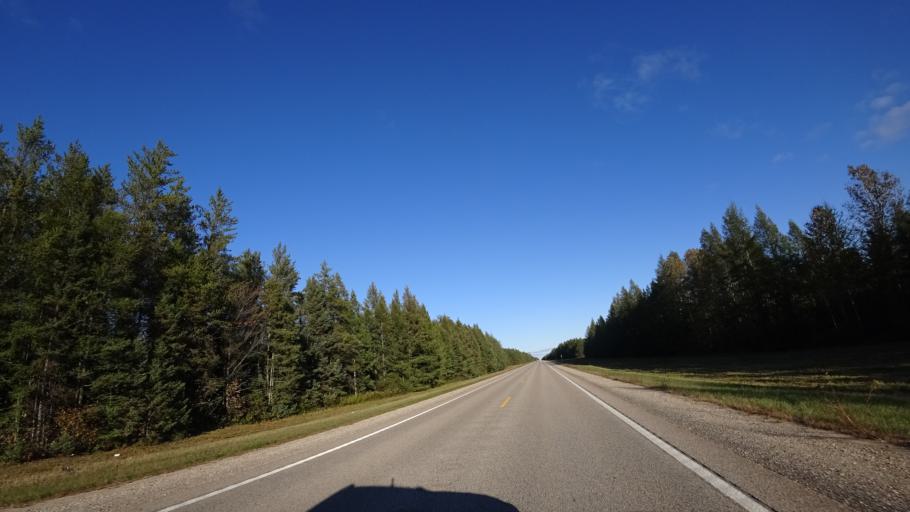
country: US
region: Michigan
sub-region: Alger County
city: Munising
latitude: 46.3464
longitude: -86.3181
